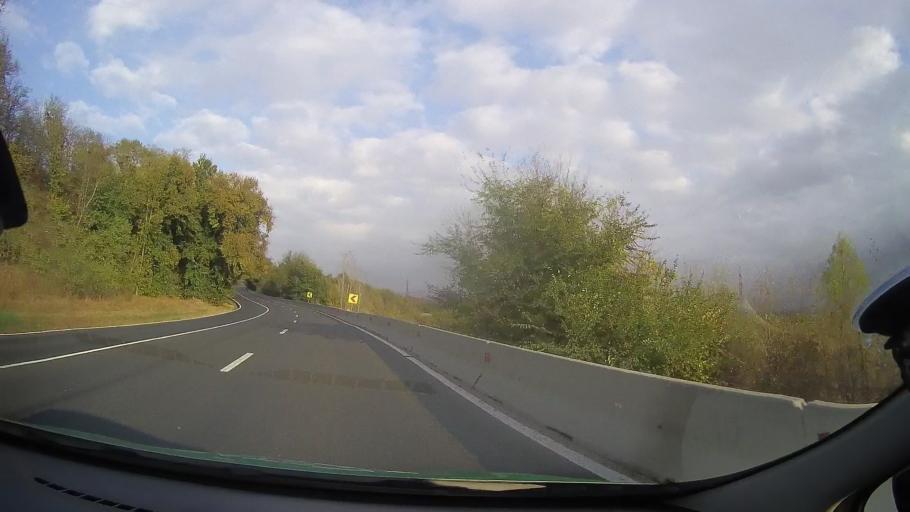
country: RO
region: Constanta
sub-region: Comuna Mircea Voda
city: Mircea Voda
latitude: 44.2698
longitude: 28.1918
